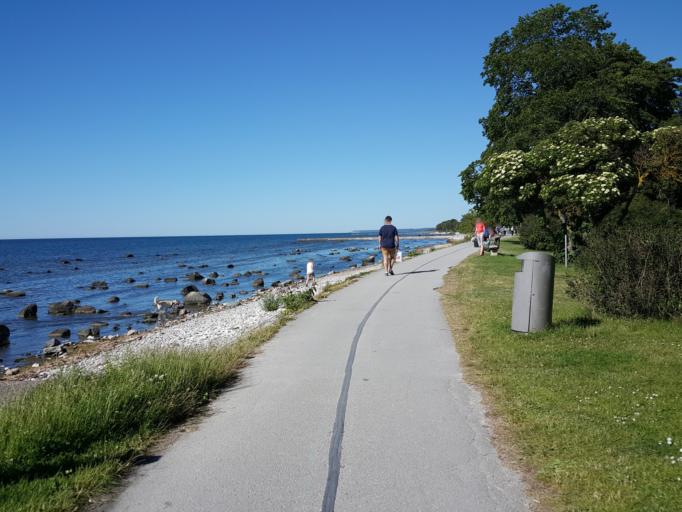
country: SE
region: Gotland
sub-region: Gotland
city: Visby
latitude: 57.6471
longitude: 18.2958
